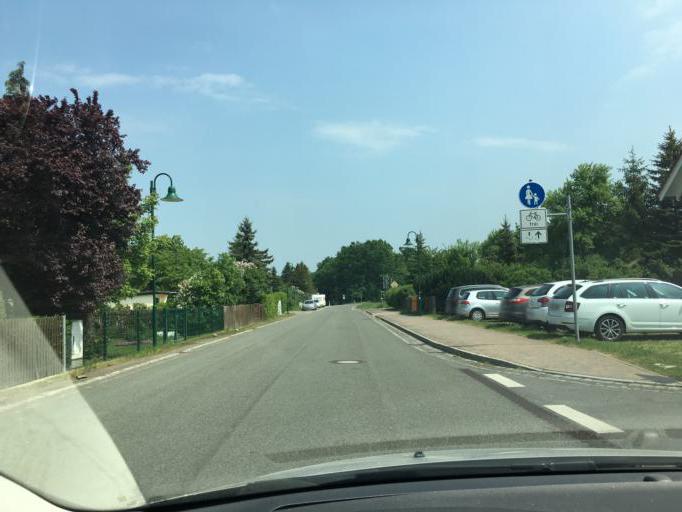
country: DE
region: Saxony
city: Naunhof
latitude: 51.2774
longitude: 12.6016
